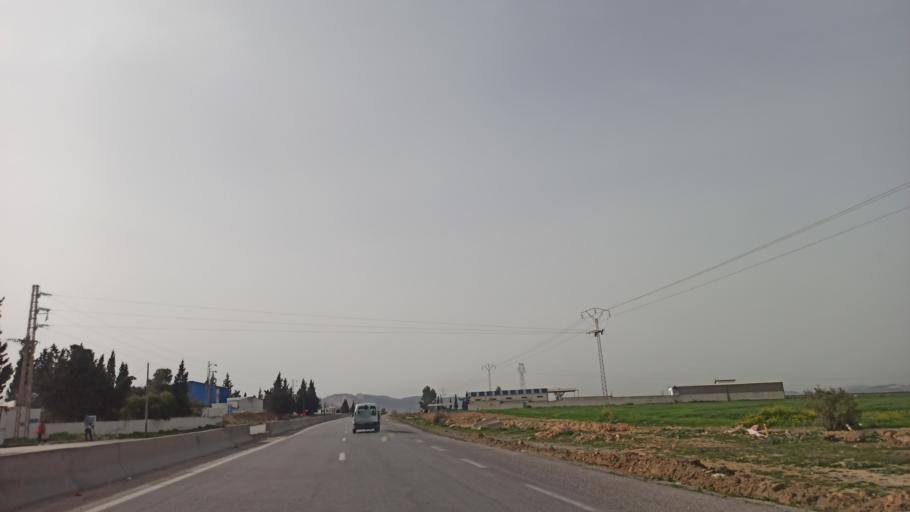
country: TN
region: Tunis
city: La Mohammedia
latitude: 36.5763
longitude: 10.0911
